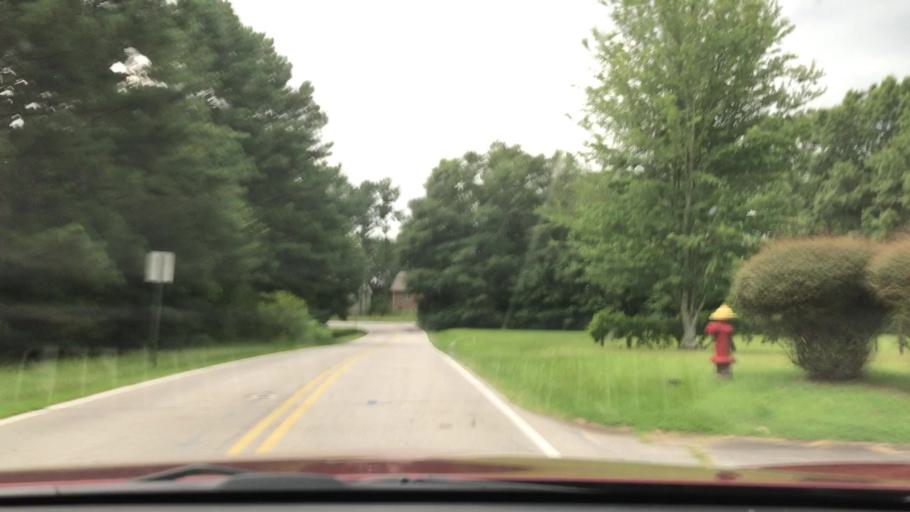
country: US
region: Georgia
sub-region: Barrow County
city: Winder
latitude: 33.9886
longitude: -83.7362
